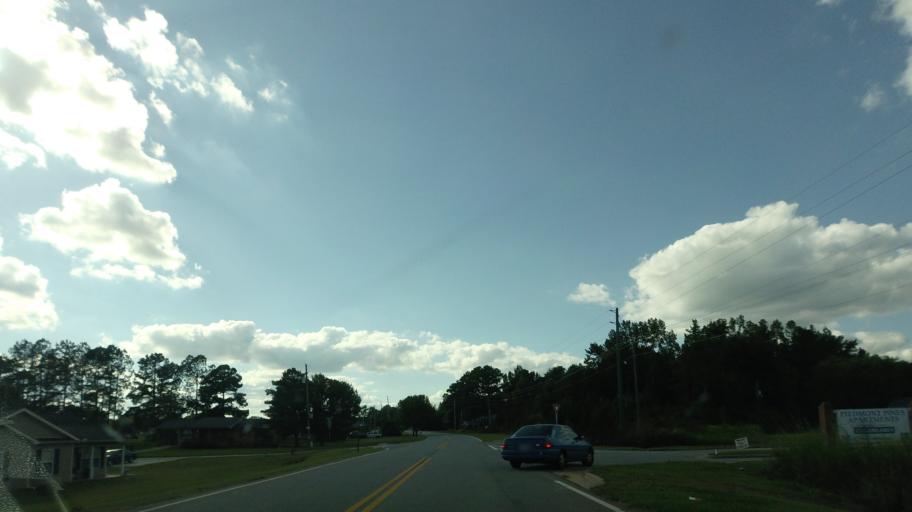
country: US
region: Georgia
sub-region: Lamar County
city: Barnesville
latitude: 33.0433
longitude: -84.1374
